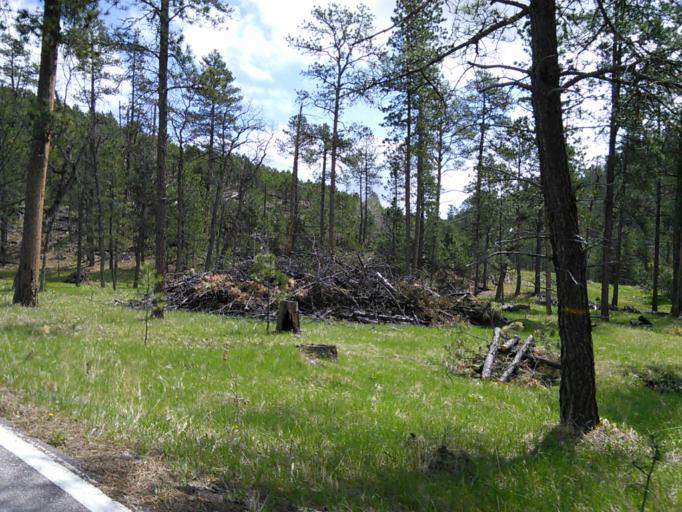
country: US
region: South Dakota
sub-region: Custer County
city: Custer
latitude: 43.7788
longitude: -103.4497
